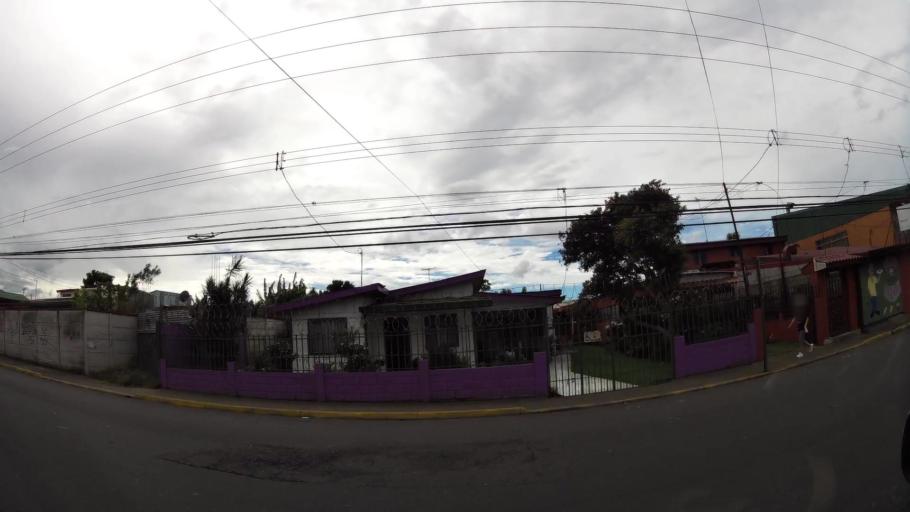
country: CR
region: San Jose
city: Ipis
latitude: 9.9738
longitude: -84.0227
